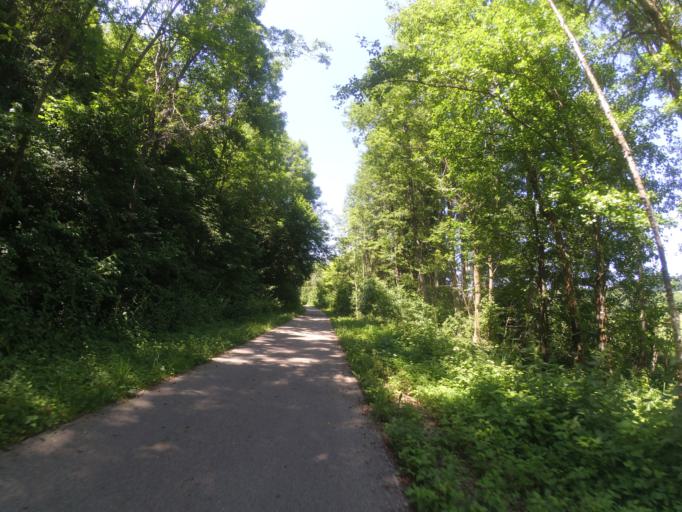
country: DE
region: Bavaria
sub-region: Swabia
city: Wald
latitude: 47.9612
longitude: 10.2900
